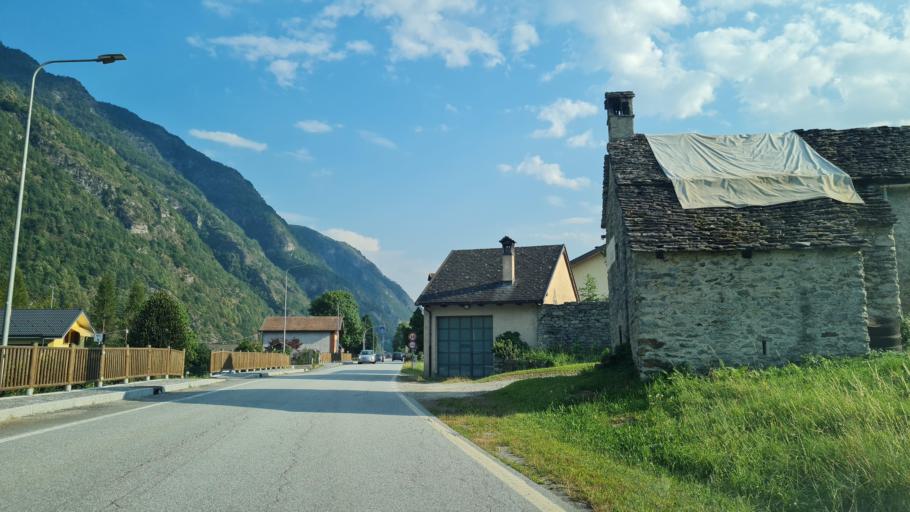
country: IT
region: Piedmont
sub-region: Provincia Verbano-Cusio-Ossola
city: Crodo
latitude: 46.2300
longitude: 8.3250
